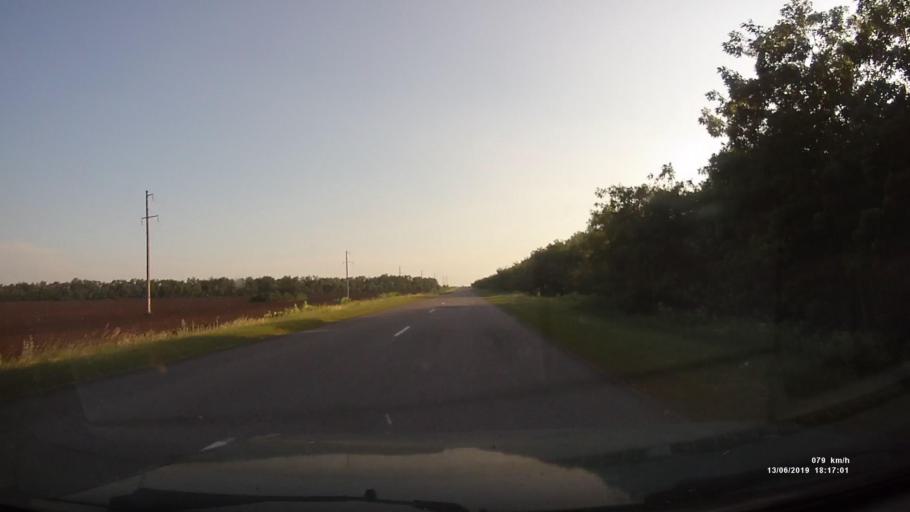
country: RU
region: Rostov
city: Kazanskaya
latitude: 49.9238
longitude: 41.3304
